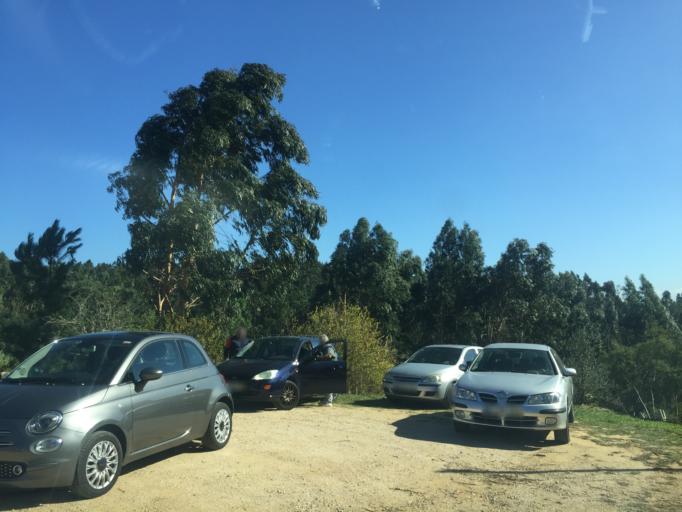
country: PT
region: Coimbra
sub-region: Figueira da Foz
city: Tavarede
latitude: 40.1833
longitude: -8.8380
